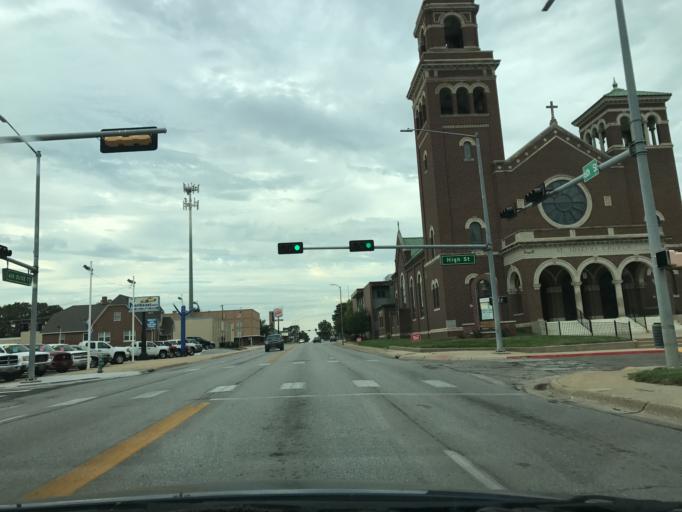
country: US
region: Nebraska
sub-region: Gage County
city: Beatrice
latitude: 40.2686
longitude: -96.7467
